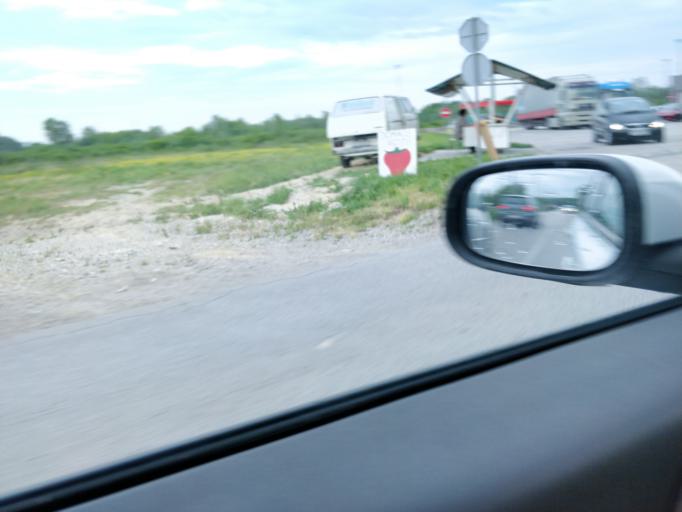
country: HR
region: Zagrebacka
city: Brckovljani
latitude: 45.7678
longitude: 16.2334
